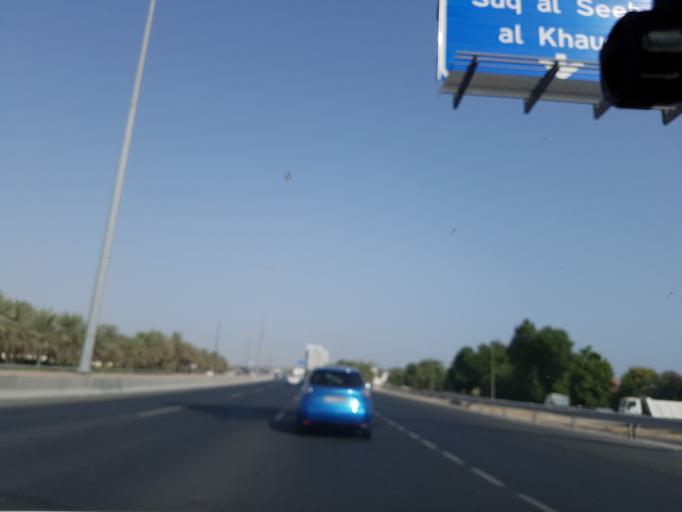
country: OM
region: Muhafazat Masqat
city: As Sib al Jadidah
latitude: 23.6511
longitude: 58.2140
